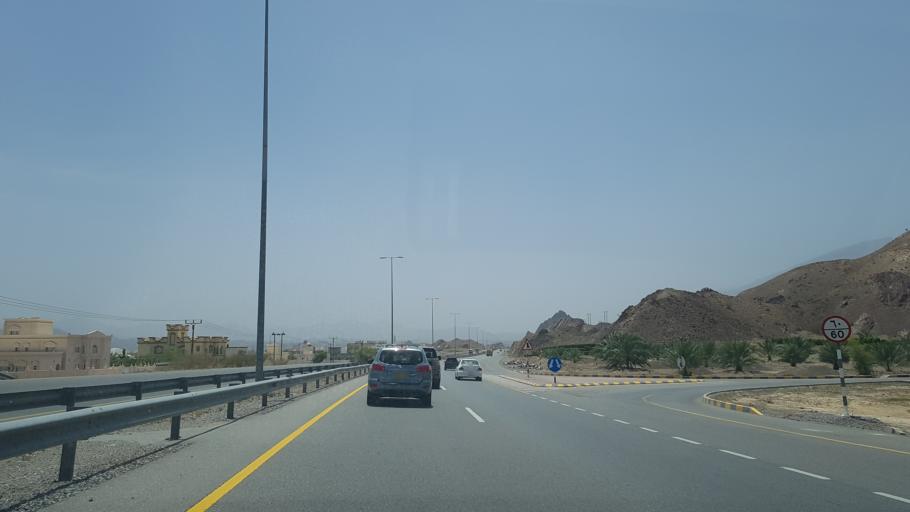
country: OM
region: Muhafazat ad Dakhiliyah
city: Sufalat Sama'il
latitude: 23.3018
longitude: 57.9421
